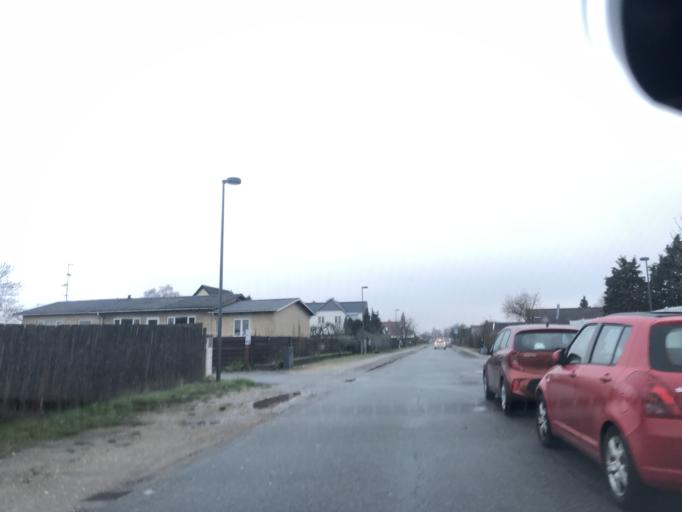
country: DK
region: Capital Region
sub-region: Tarnby Kommune
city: Tarnby
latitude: 55.6384
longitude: 12.5922
